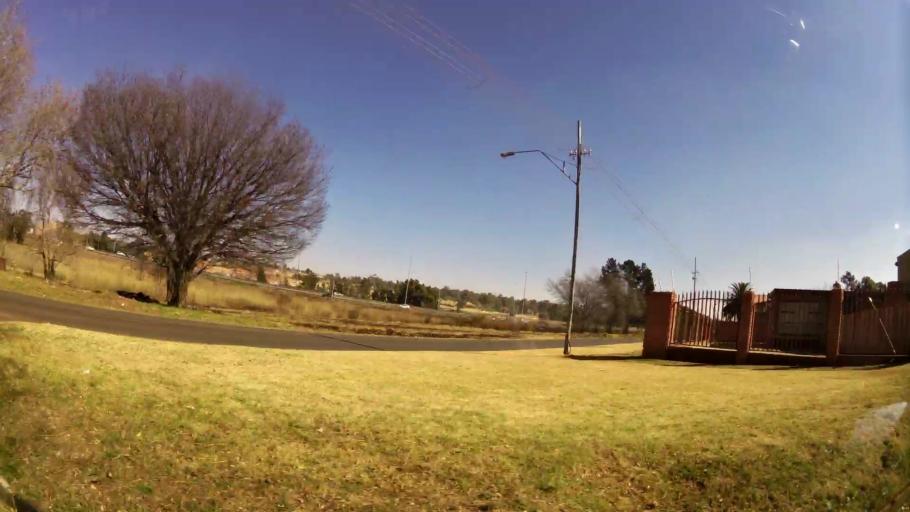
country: ZA
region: Gauteng
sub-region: City of Johannesburg Metropolitan Municipality
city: Roodepoort
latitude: -26.1890
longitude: 27.9497
